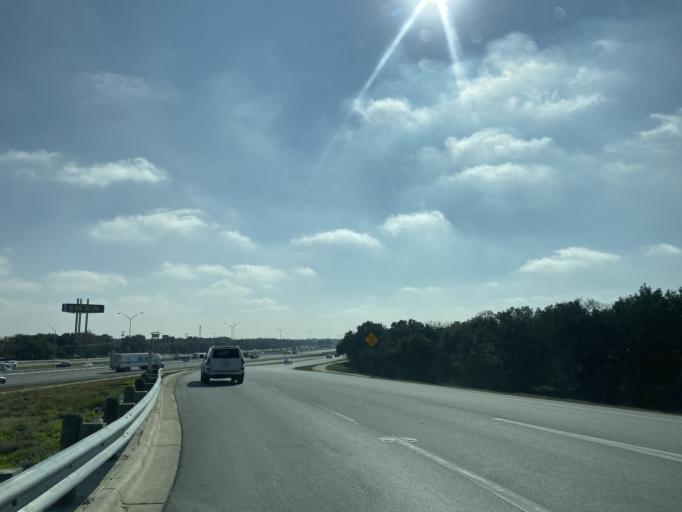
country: US
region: Texas
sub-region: Williamson County
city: Round Rock
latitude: 30.5576
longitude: -97.6934
